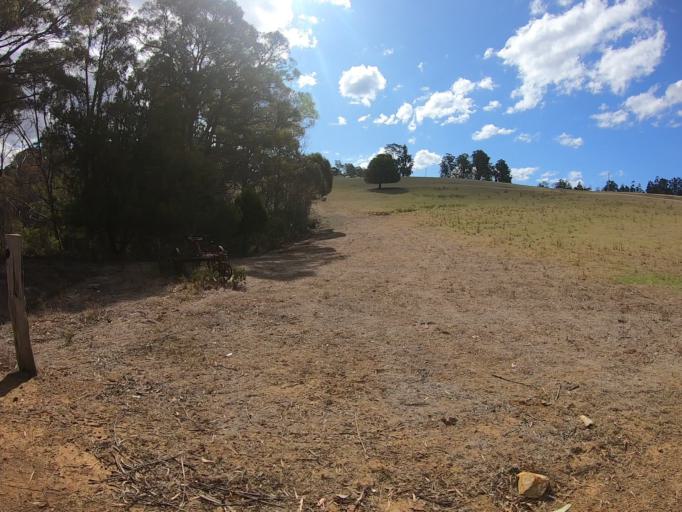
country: AU
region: Tasmania
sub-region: Brighton
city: Bridgewater
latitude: -42.4969
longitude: 147.4221
